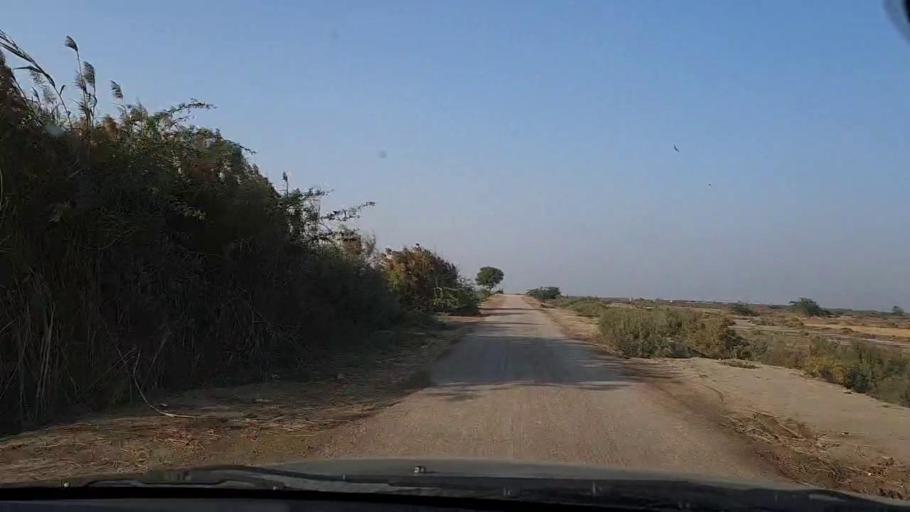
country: PK
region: Sindh
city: Chuhar Jamali
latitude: 24.3052
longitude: 67.7555
